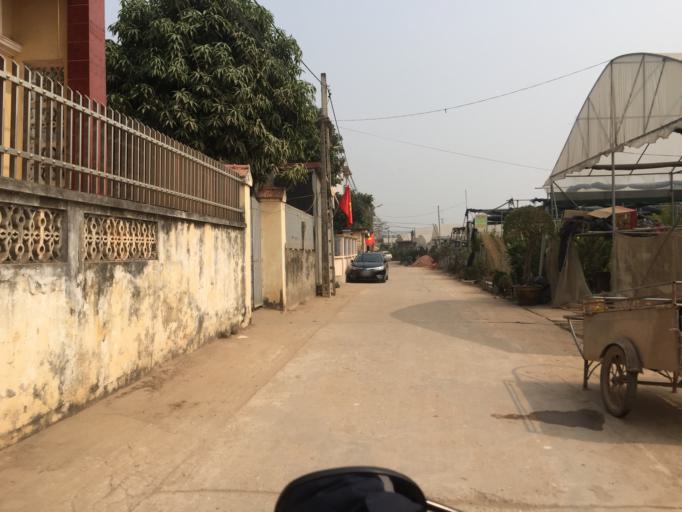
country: VN
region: Hung Yen
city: Van Giang
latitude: 20.9696
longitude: 105.9159
